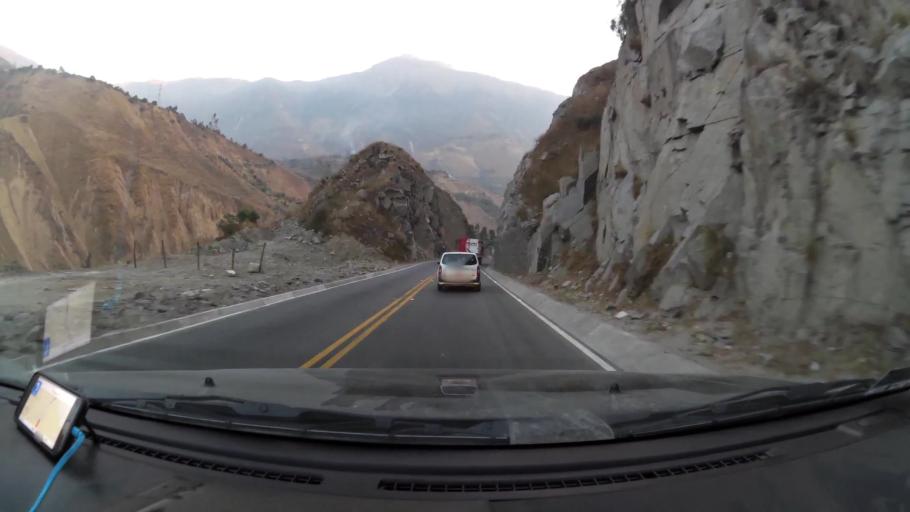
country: PE
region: Lima
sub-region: Provincia de Huarochiri
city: Surco
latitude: -11.8787
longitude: -76.4339
